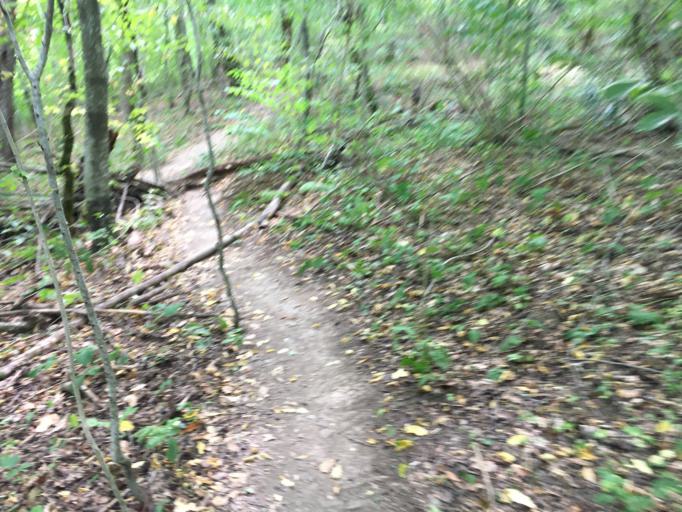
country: RU
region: Krasnodarskiy
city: Tuapse
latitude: 44.2547
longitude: 39.2263
